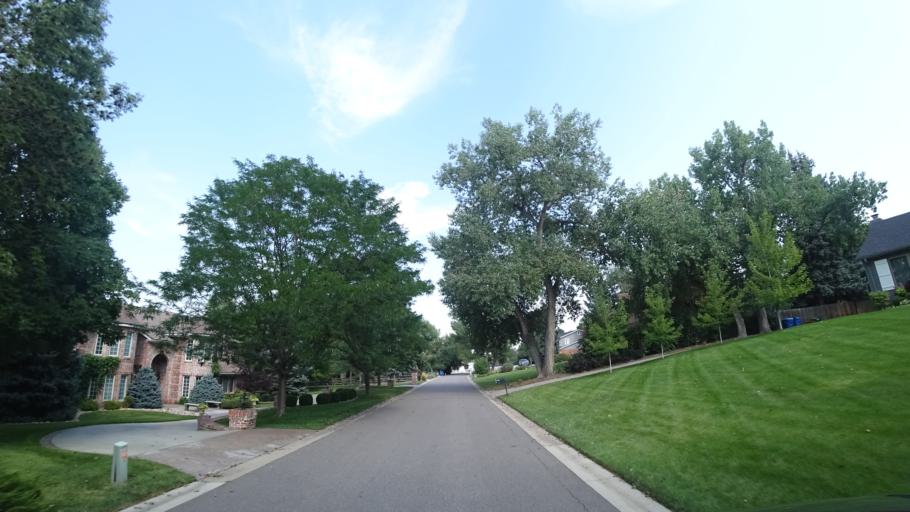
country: US
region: Colorado
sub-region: Arapahoe County
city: Greenwood Village
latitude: 39.6171
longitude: -104.9631
